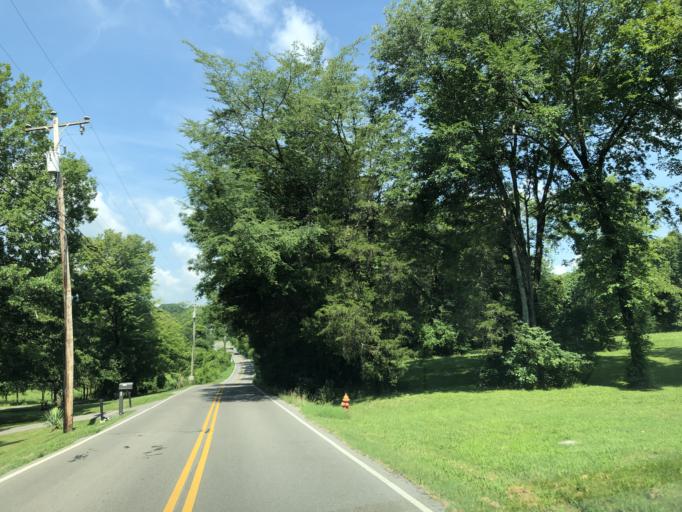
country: US
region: Tennessee
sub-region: Williamson County
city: Nolensville
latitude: 36.0140
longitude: -86.6747
